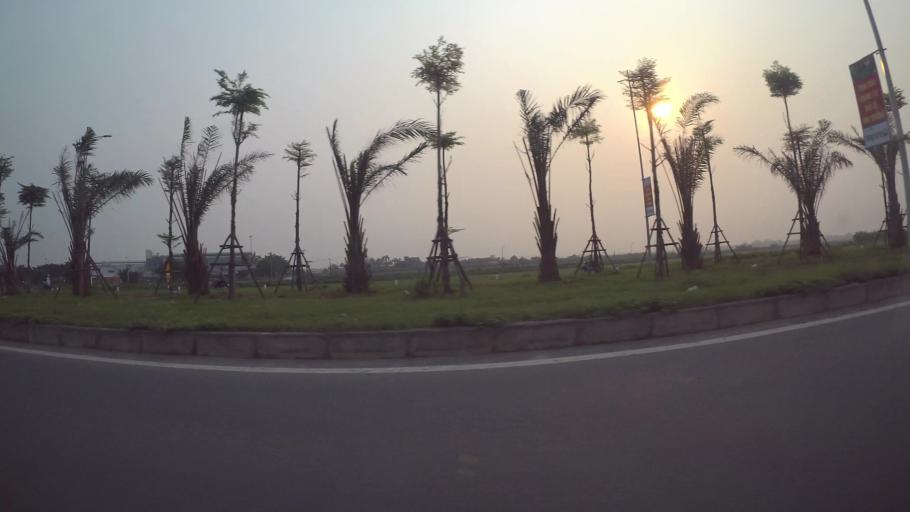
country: VN
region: Ha Noi
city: Kim Bai
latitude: 20.8746
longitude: 105.8024
